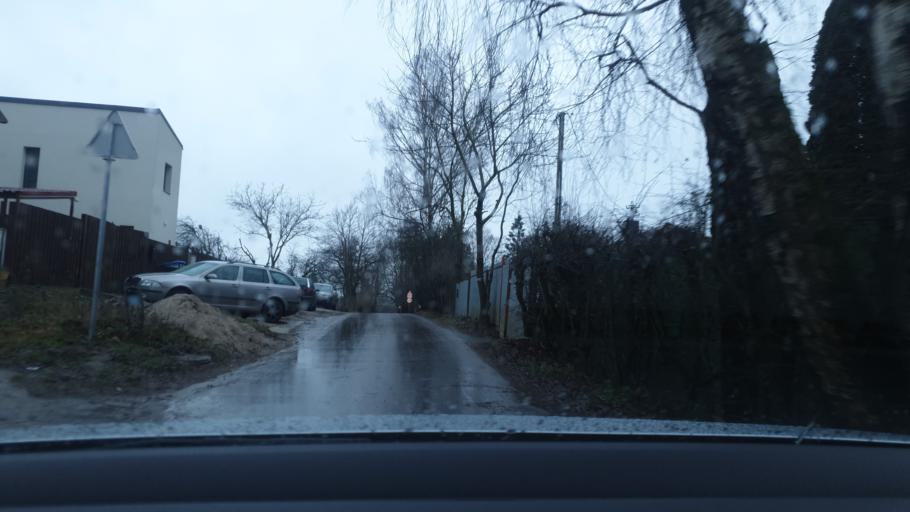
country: LT
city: Skaidiskes
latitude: 54.7055
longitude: 25.4088
